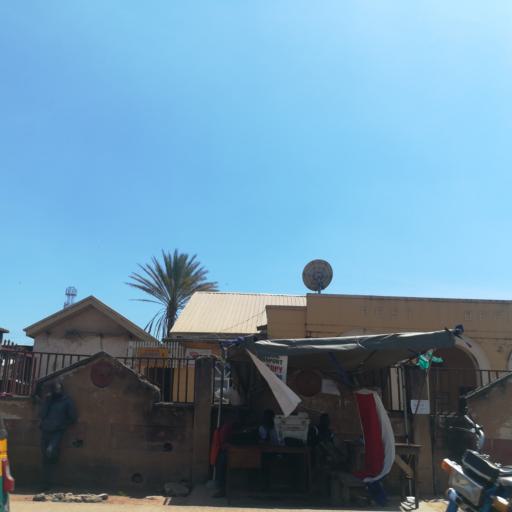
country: NG
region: Plateau
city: Bukuru
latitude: 9.7953
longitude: 8.8658
